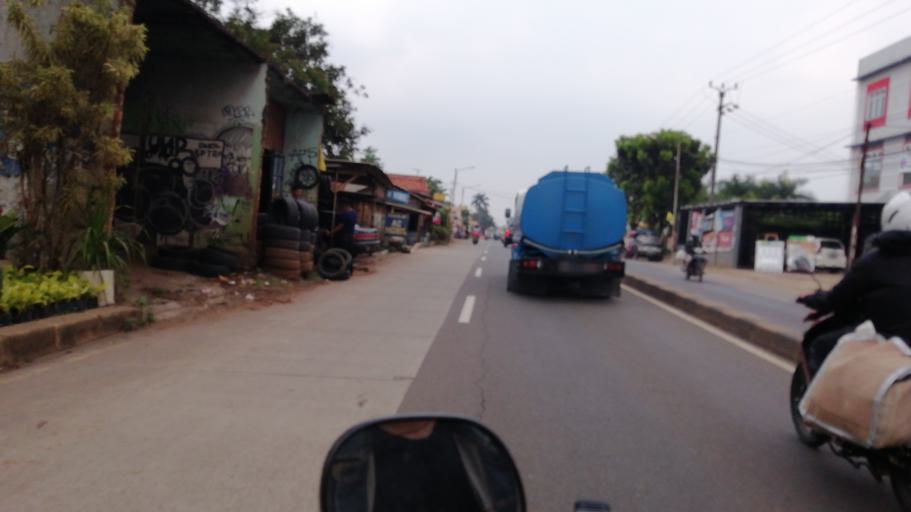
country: ID
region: West Java
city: Parung
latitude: -6.4553
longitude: 106.7310
